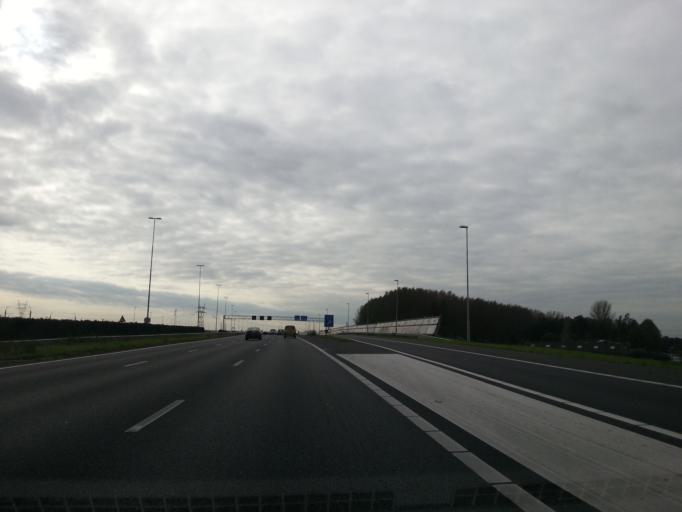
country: NL
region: South Holland
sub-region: Gemeente Leiderdorp
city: Leiderdorp
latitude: 52.1692
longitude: 4.5643
